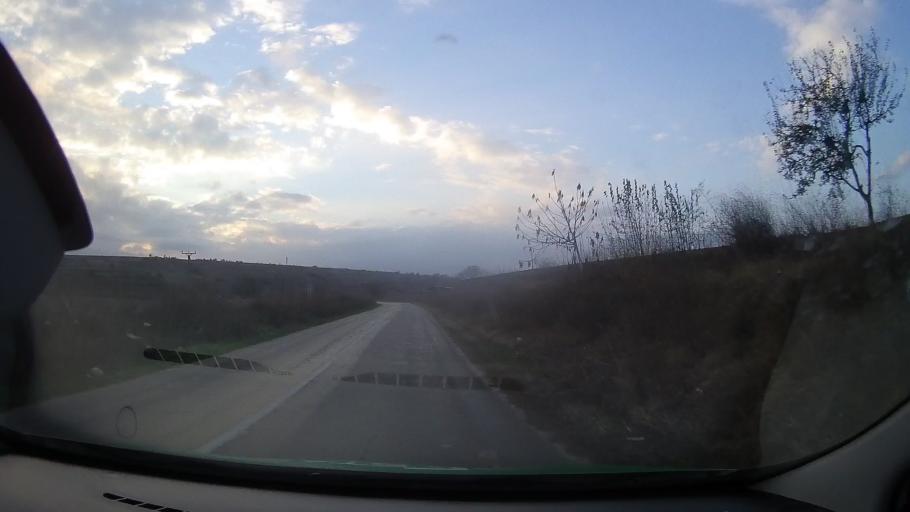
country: RO
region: Constanta
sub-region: Comuna Baneasa
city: Baneasa
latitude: 44.0595
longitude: 27.7128
